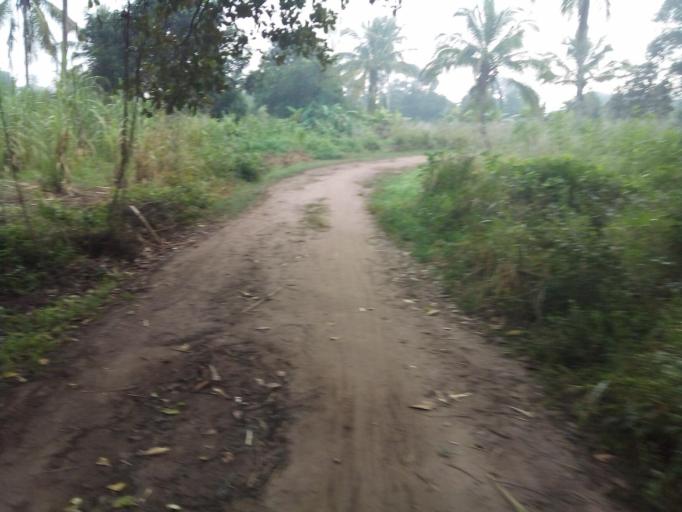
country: MZ
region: Zambezia
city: Quelimane
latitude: -17.5881
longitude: 36.6847
